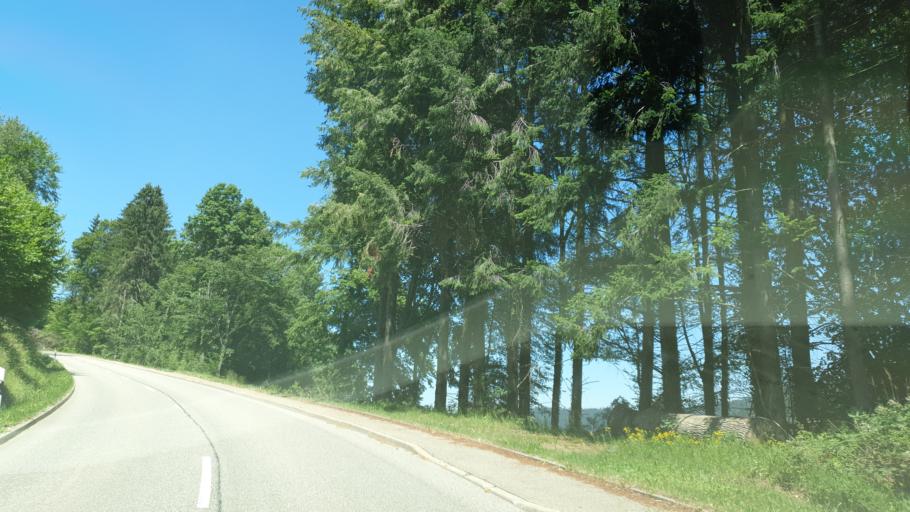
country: DE
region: Baden-Wuerttemberg
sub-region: Freiburg Region
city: Horben
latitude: 47.9396
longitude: 7.8637
